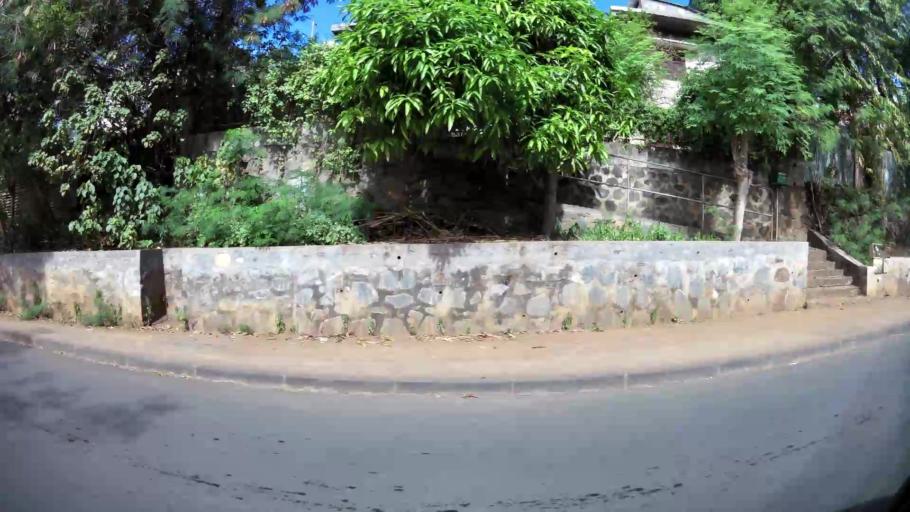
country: YT
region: Mamoudzou
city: Mamoudzou
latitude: -12.7857
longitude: 45.2219
